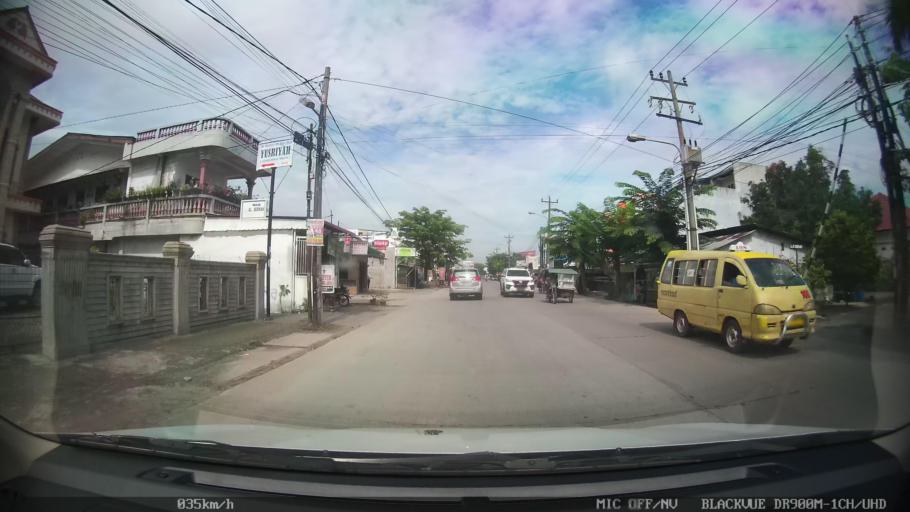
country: ID
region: North Sumatra
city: Sunggal
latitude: 3.6057
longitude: 98.6200
